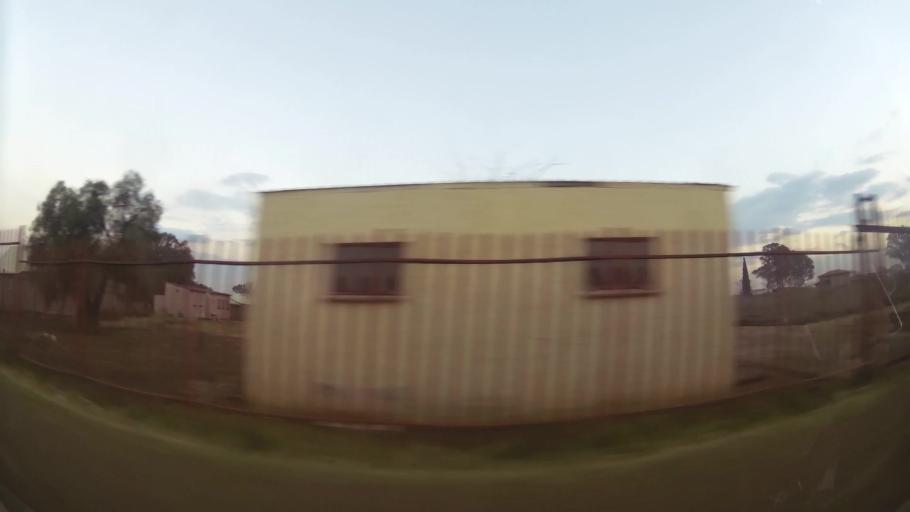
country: ZA
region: Gauteng
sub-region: City of Johannesburg Metropolitan Municipality
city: Orange Farm
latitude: -26.5488
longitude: 27.8589
